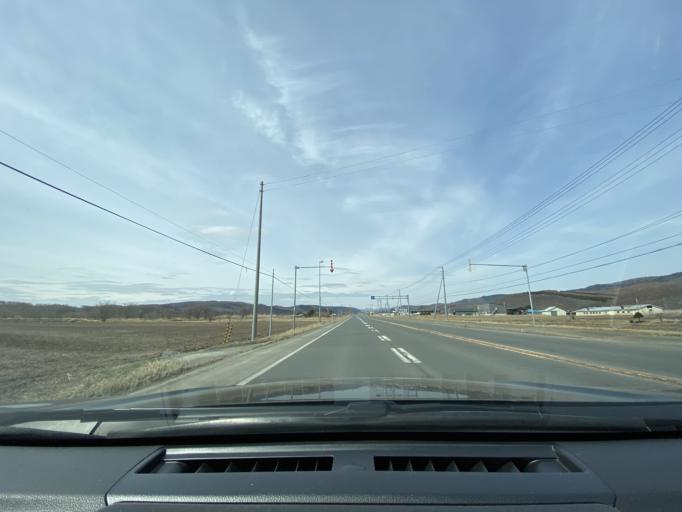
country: JP
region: Hokkaido
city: Kitami
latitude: 43.7949
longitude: 143.7294
